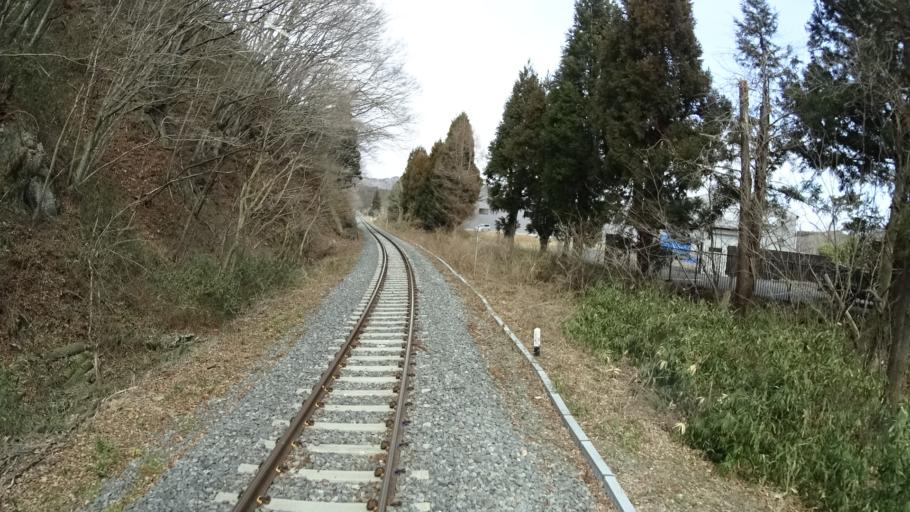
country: JP
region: Iwate
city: Miyako
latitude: 39.5568
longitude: 141.9400
